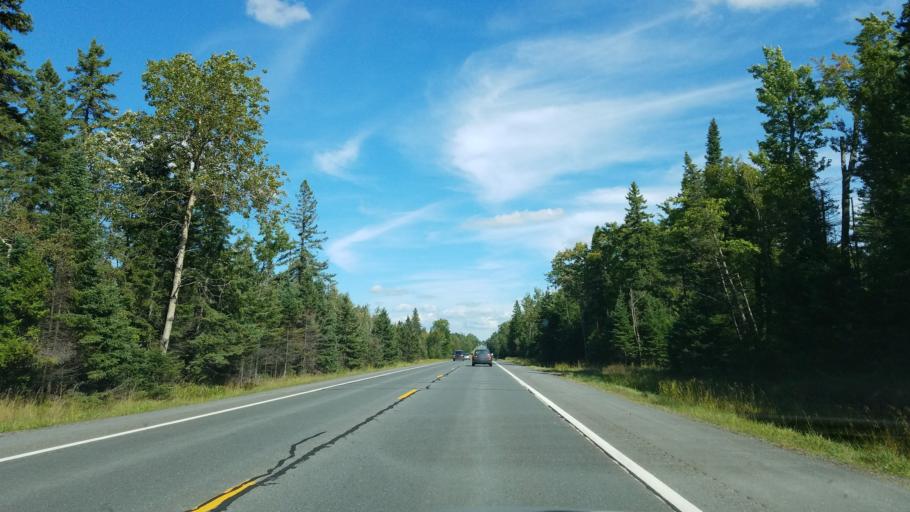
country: US
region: Michigan
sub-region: Baraga County
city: L'Anse
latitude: 46.5788
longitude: -88.4216
